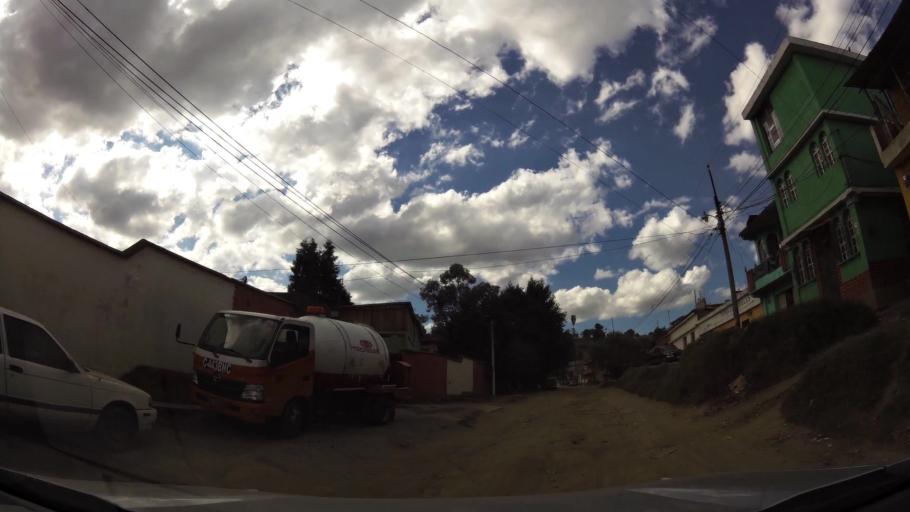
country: GT
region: Quetzaltenango
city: Quetzaltenango
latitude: 14.8407
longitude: -91.5388
